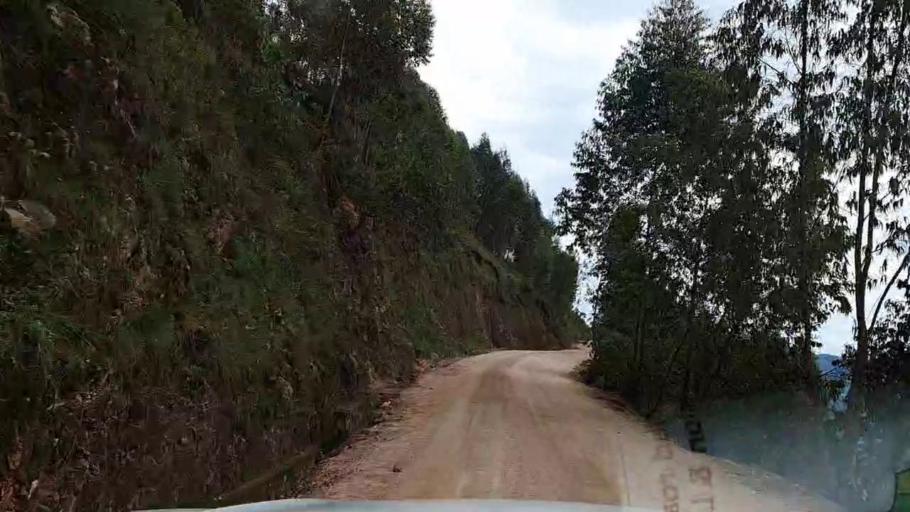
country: RW
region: Southern Province
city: Nzega
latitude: -2.3690
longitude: 29.4507
